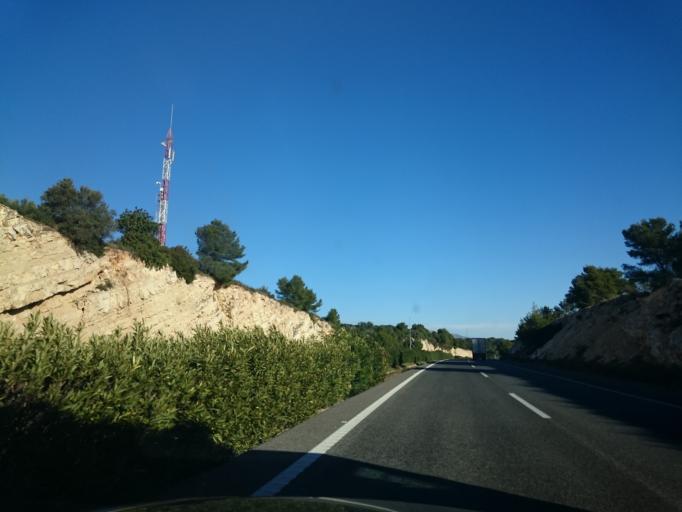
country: ES
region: Catalonia
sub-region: Provincia de Tarragona
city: L'Ampolla
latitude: 40.8421
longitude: 0.7458
